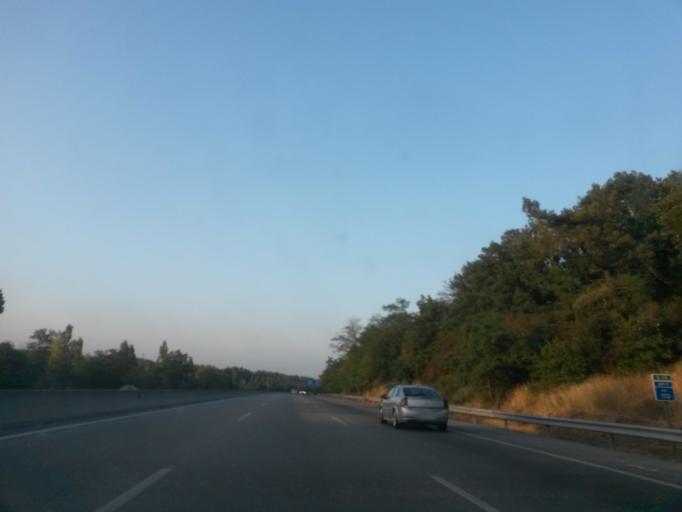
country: ES
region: Catalonia
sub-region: Provincia de Barcelona
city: Sant Celoni
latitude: 41.6649
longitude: 2.4677
